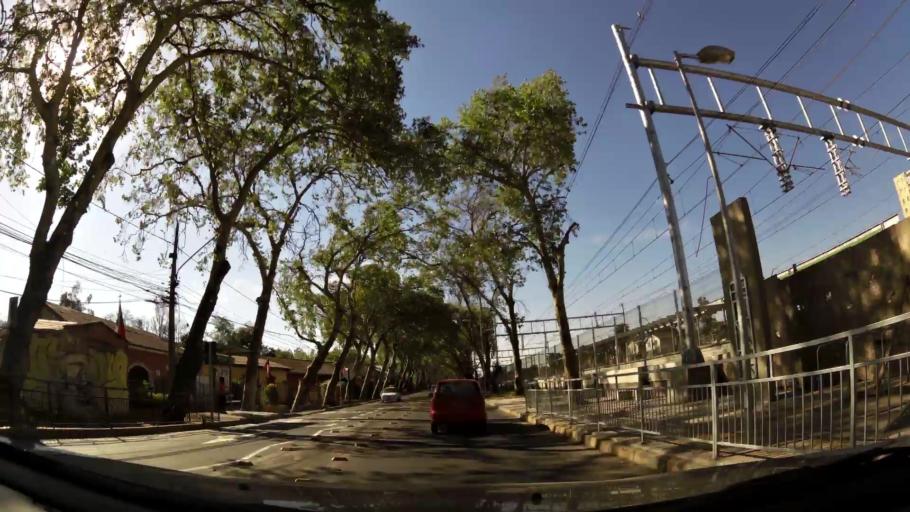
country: CL
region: Santiago Metropolitan
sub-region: Provincia de Maipo
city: San Bernardo
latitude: -33.6069
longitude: -70.6972
